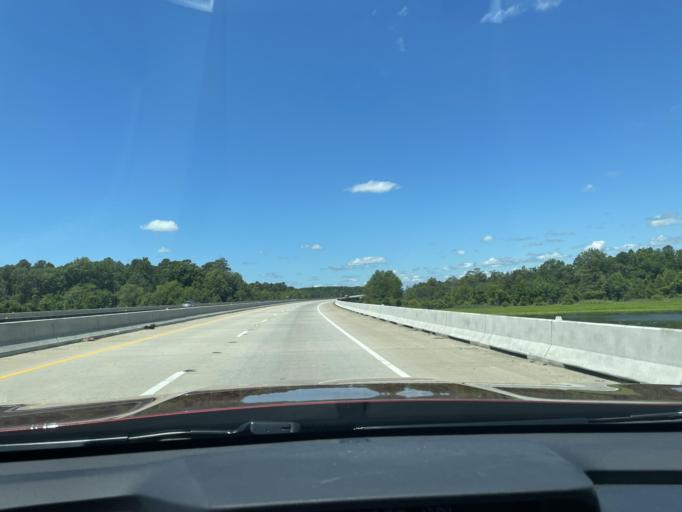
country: US
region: Arkansas
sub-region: Jefferson County
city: Pine Bluff
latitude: 34.1712
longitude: -91.9984
